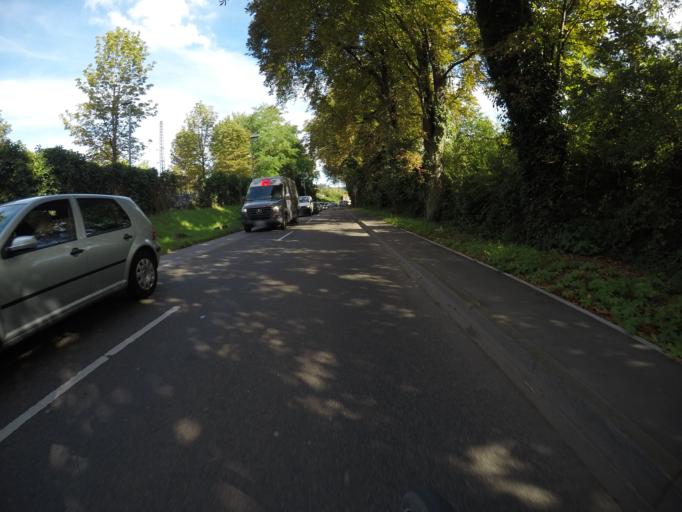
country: DE
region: Baden-Wuerttemberg
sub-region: Regierungsbezirk Stuttgart
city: Stuttgart-Ost
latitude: 48.7971
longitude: 9.2355
